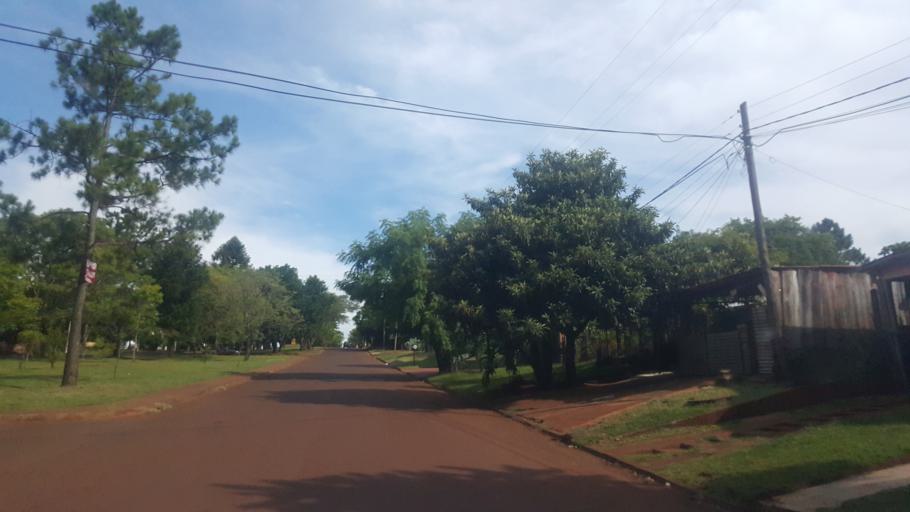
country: AR
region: Misiones
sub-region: Departamento de Leandro N. Alem
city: Leandro N. Alem
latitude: -27.5984
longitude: -55.3322
